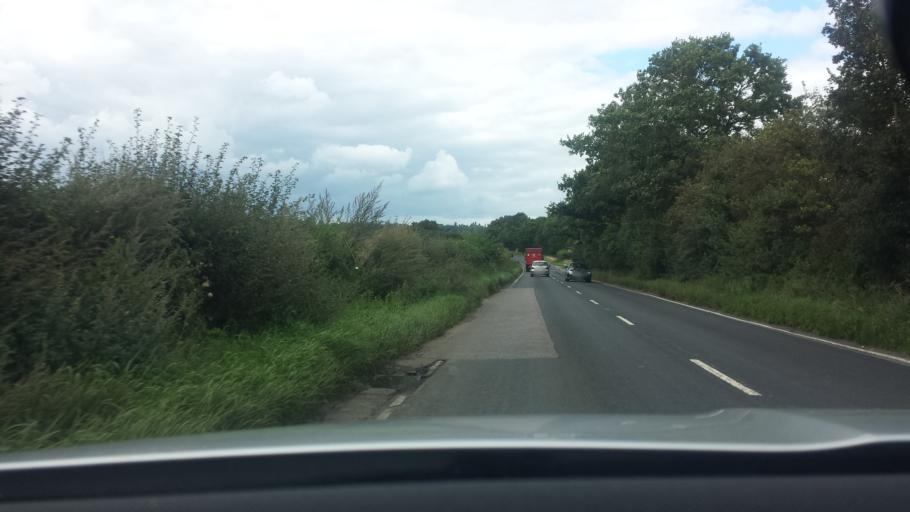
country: GB
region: England
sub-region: Kent
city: Marden
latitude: 51.2043
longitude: 0.5171
